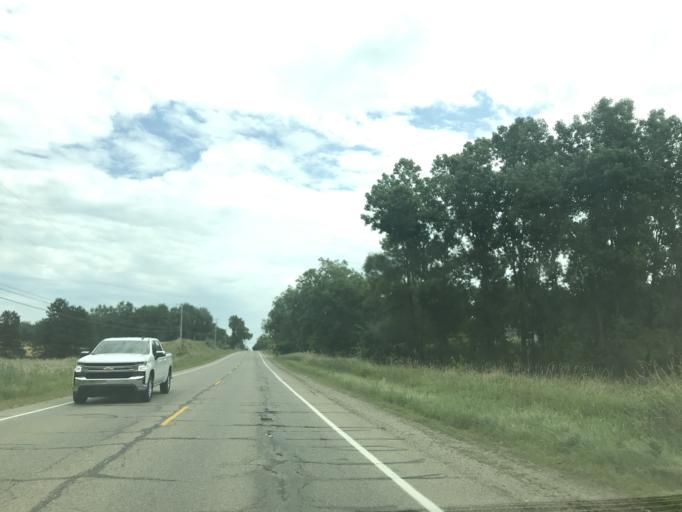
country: US
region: Michigan
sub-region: Clinton County
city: Wacousta
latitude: 42.7917
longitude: -84.7060
